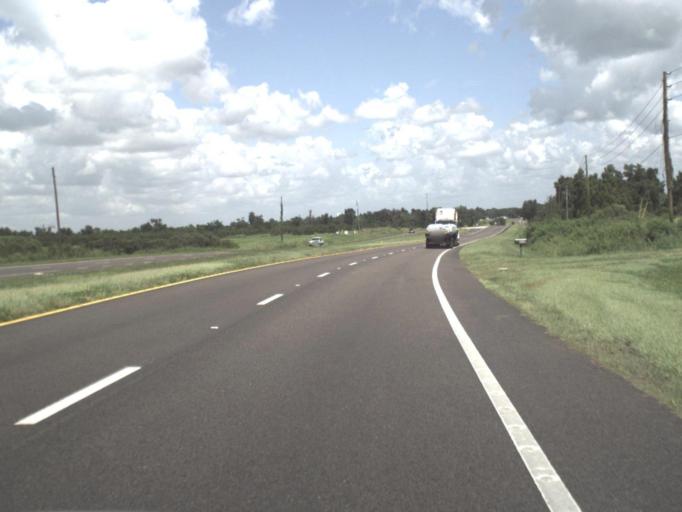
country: US
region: Florida
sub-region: Hardee County
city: Bowling Green
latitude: 27.6136
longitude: -81.8263
